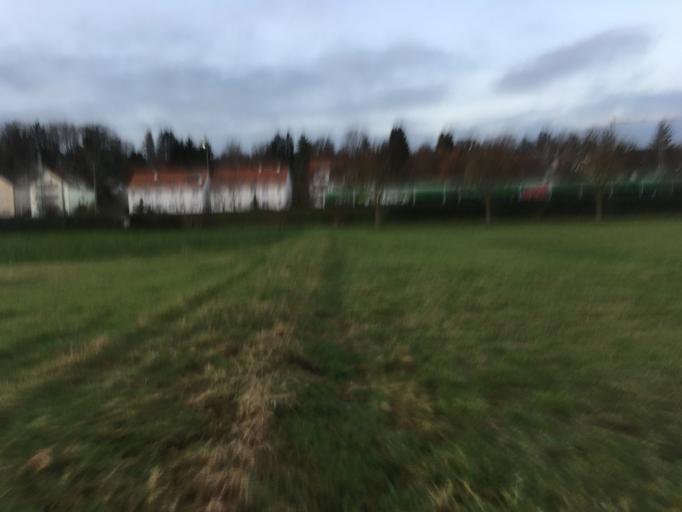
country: DE
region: Baden-Wuerttemberg
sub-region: Regierungsbezirk Stuttgart
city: Flein
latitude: 49.1246
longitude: 9.1834
